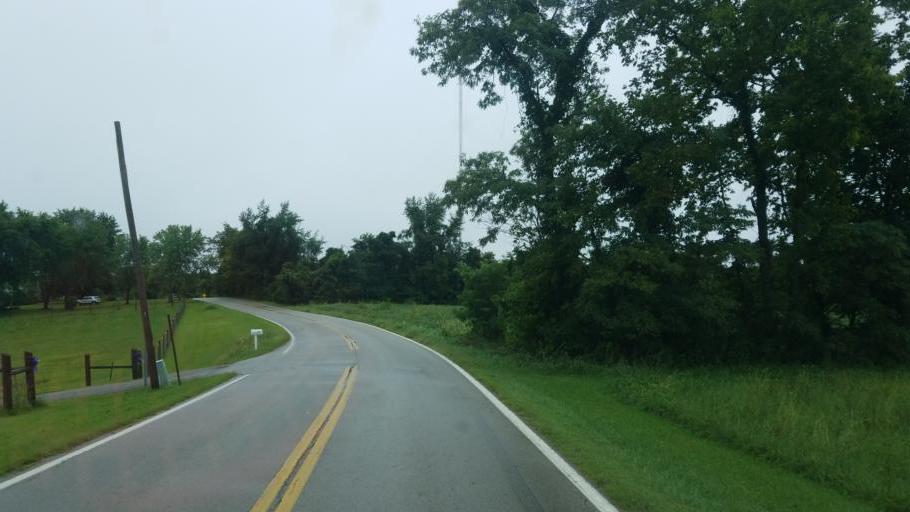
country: US
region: Ohio
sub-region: Adams County
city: West Union
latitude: 38.7322
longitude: -83.5177
